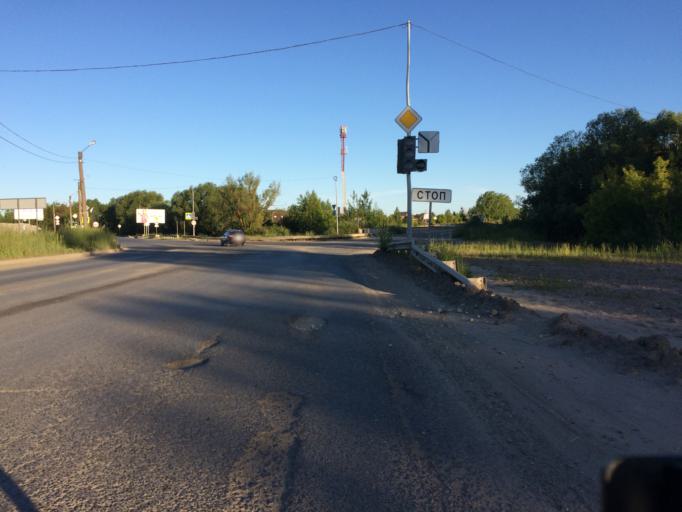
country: RU
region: Mariy-El
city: Medvedevo
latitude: 56.6534
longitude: 47.8417
